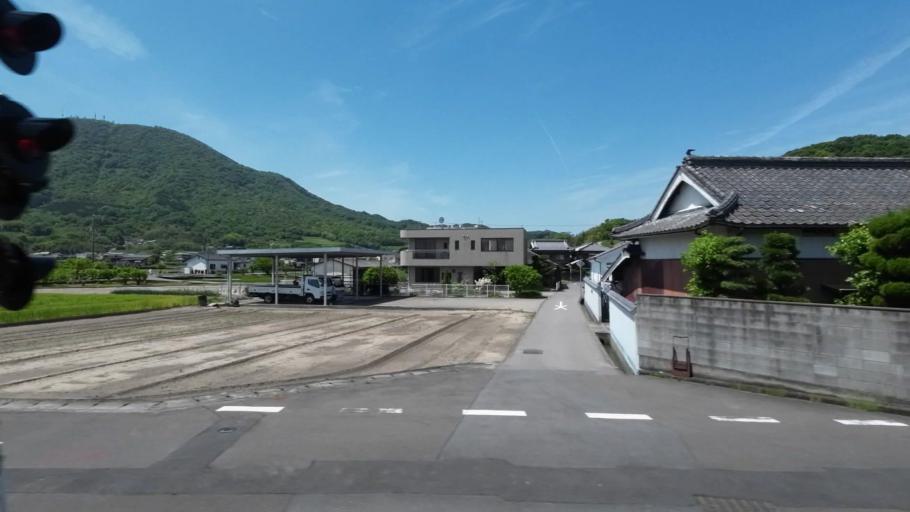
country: JP
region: Kagawa
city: Marugame
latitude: 34.2192
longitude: 133.7967
